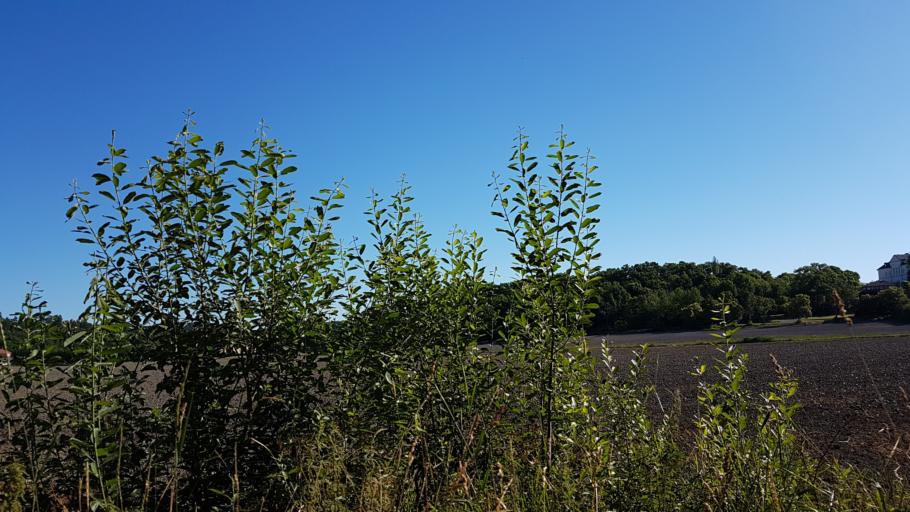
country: SE
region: OEstergoetland
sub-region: Valdemarsviks Kommun
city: Gusum
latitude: 58.4278
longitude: 16.5869
